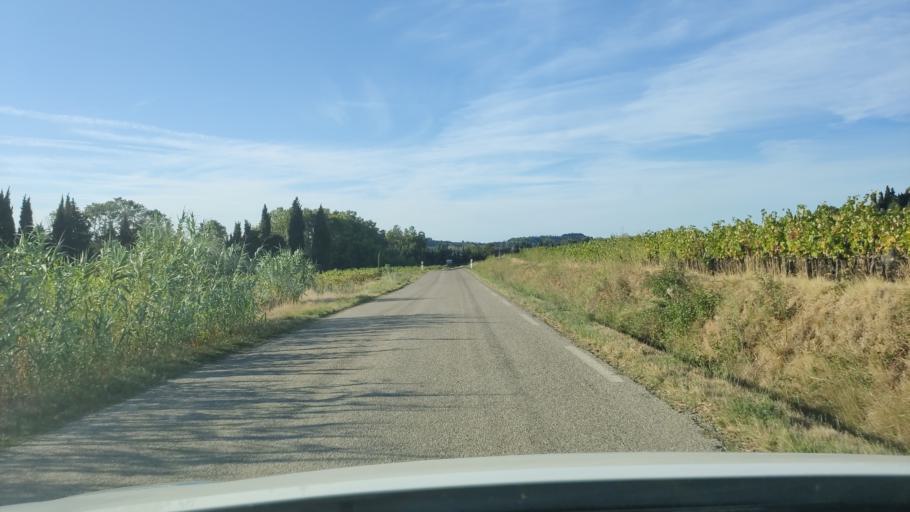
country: FR
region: Languedoc-Roussillon
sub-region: Departement du Gard
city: Saze
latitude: 43.9432
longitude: 4.6532
